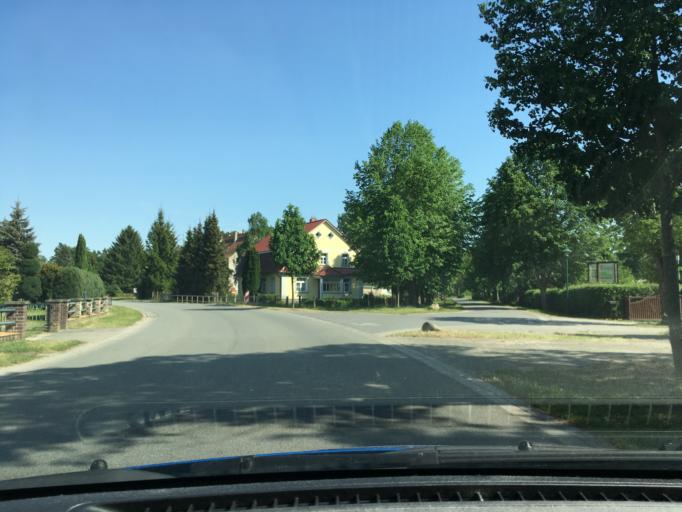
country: DE
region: Lower Saxony
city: Hitzacker
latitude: 53.1914
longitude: 11.0465
